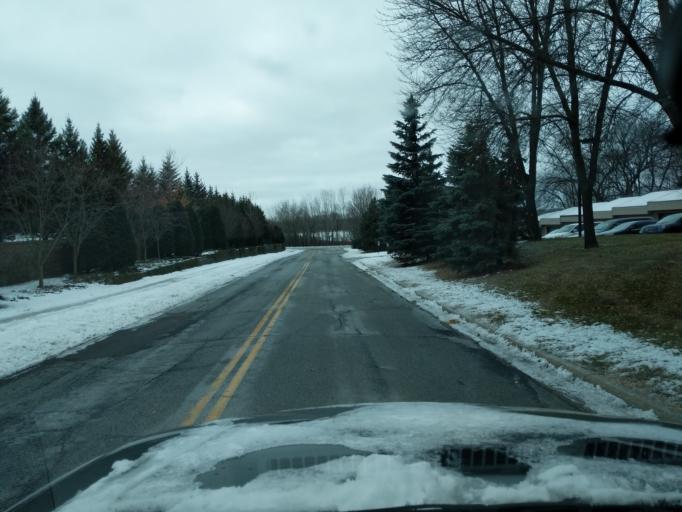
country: US
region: Minnesota
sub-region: Hennepin County
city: Eden Prairie
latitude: 44.8515
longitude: -93.4348
